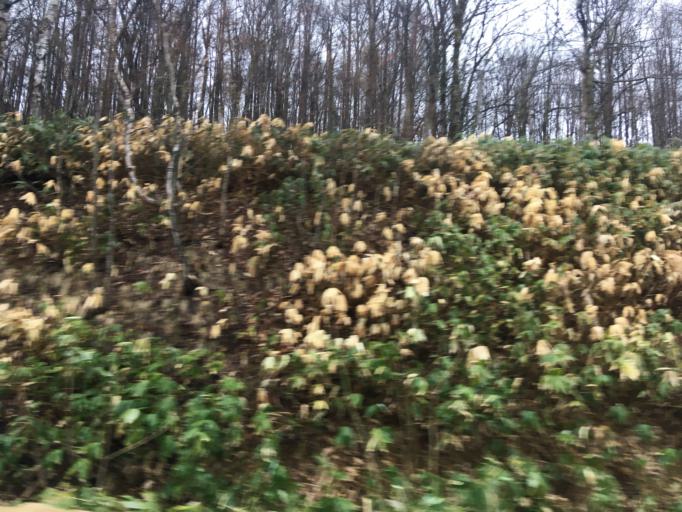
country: JP
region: Hokkaido
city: Nayoro
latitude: 44.0756
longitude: 142.4168
